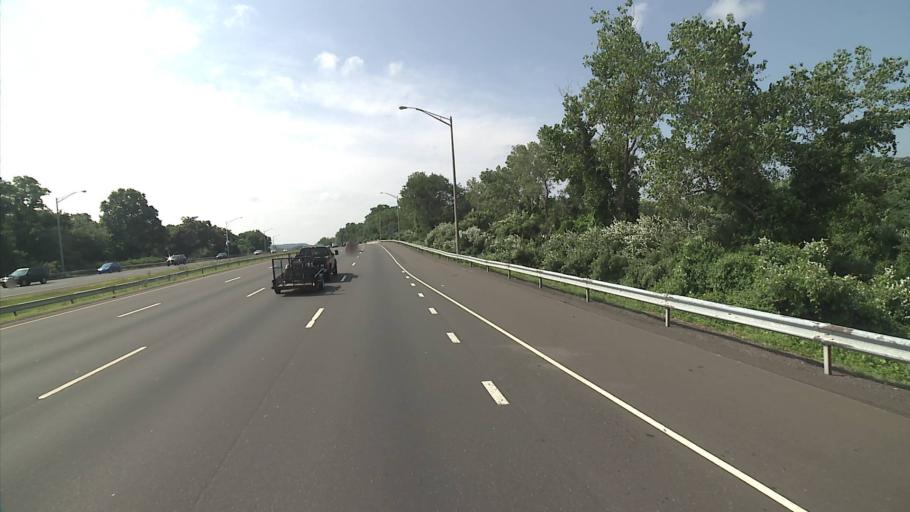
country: US
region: Connecticut
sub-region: New Haven County
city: North Haven
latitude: 41.3695
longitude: -72.8700
